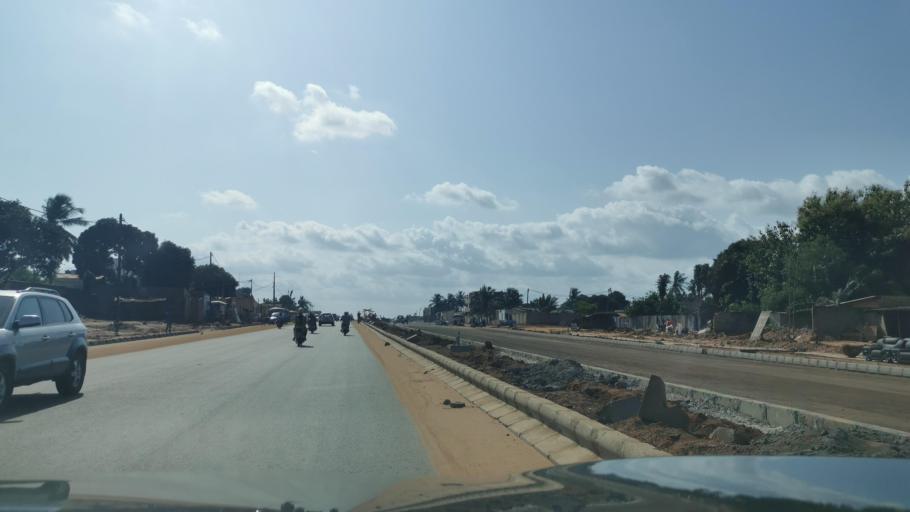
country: TG
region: Maritime
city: Lome
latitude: 6.2165
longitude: 1.1299
